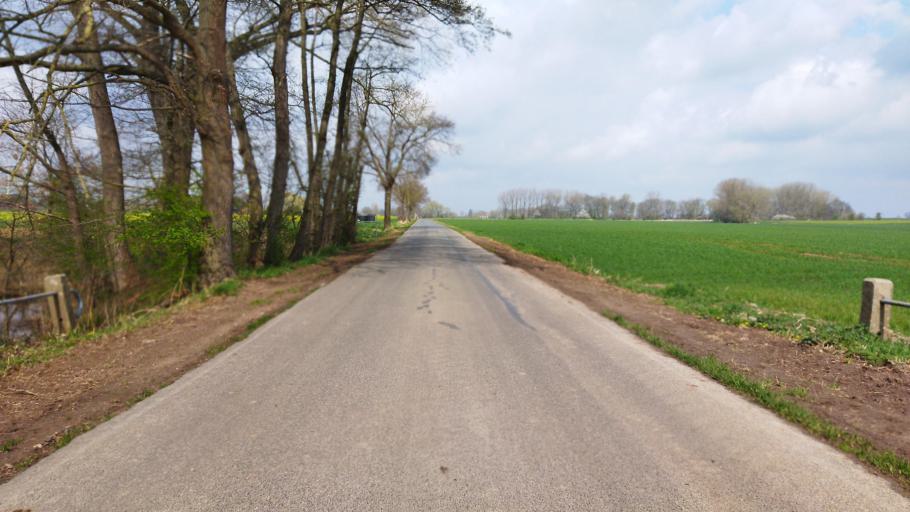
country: DE
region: Lower Saxony
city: Hilgermissen
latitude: 52.8414
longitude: 9.1898
